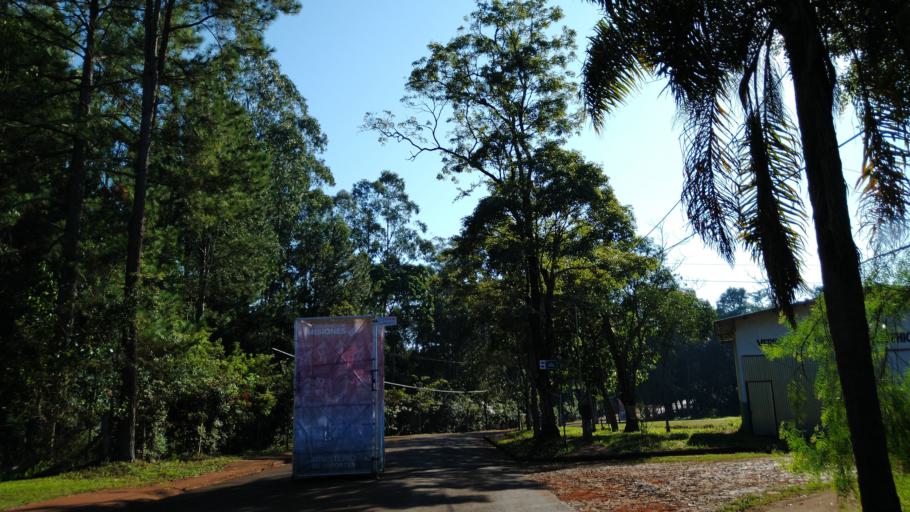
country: AR
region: Misiones
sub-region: Departamento de Montecarlo
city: Montecarlo
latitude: -26.5570
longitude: -54.7747
